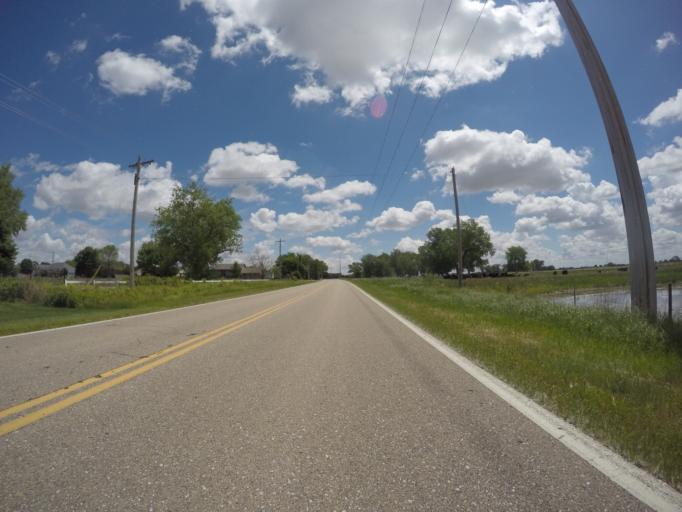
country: US
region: Nebraska
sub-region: Buffalo County
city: Kearney
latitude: 40.6535
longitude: -99.0931
